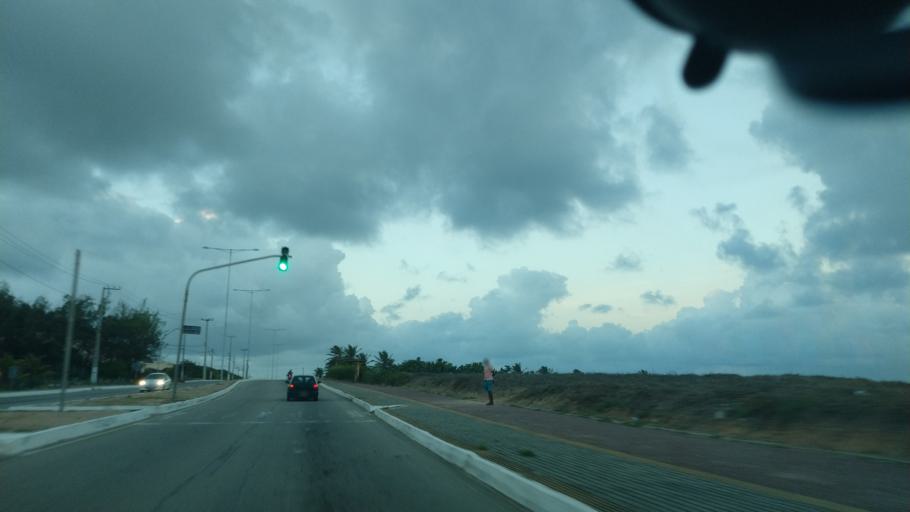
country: BR
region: Rio Grande do Norte
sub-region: Natal
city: Natal
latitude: -5.8004
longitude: -35.1826
